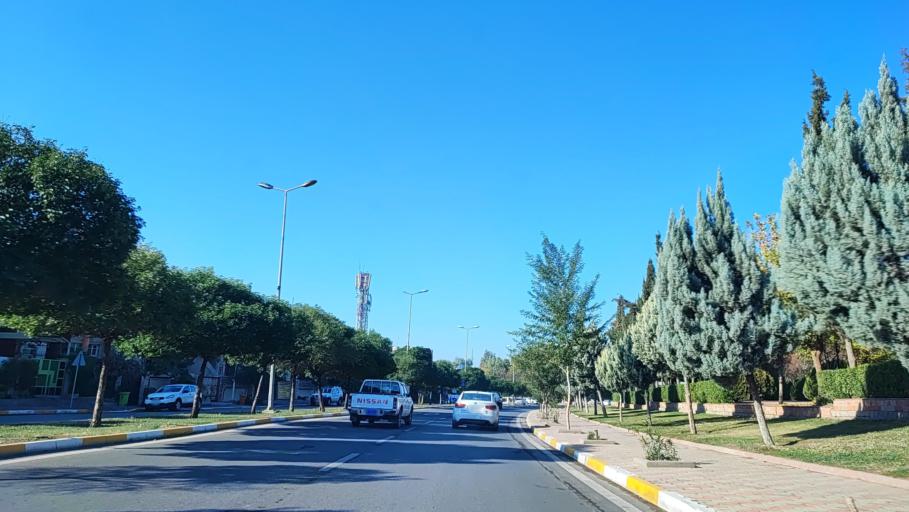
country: IQ
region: Arbil
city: Erbil
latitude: 36.1797
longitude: 44.0048
